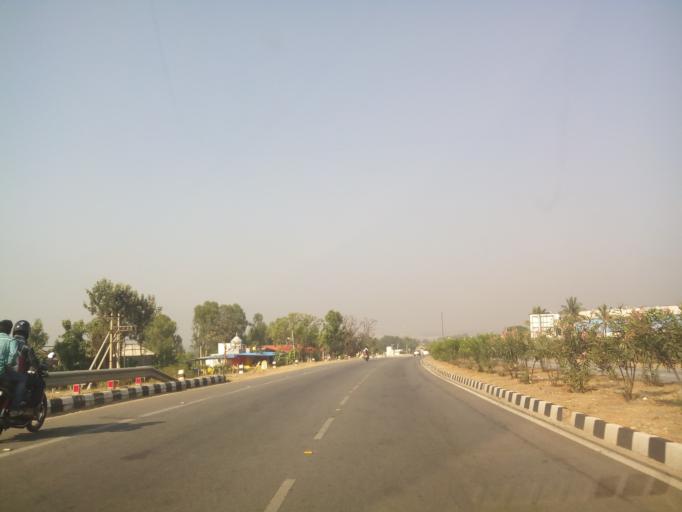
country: IN
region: Karnataka
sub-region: Bangalore Rural
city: Nelamangala
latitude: 13.0665
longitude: 77.3579
